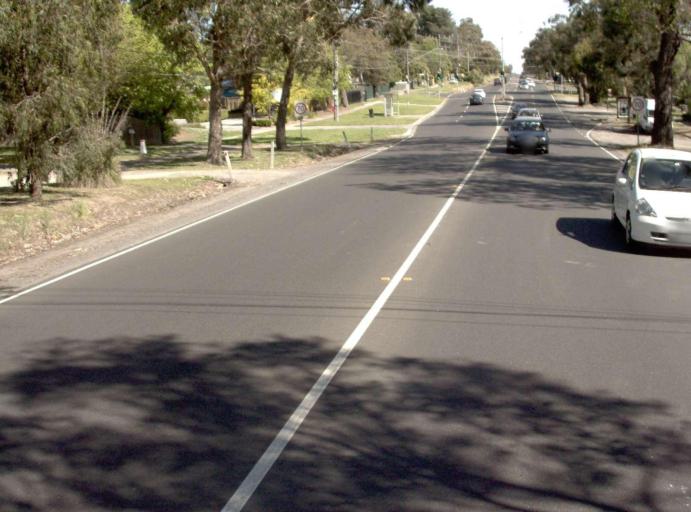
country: AU
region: Victoria
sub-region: Maroondah
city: Croydon South
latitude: -37.8168
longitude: 145.2692
